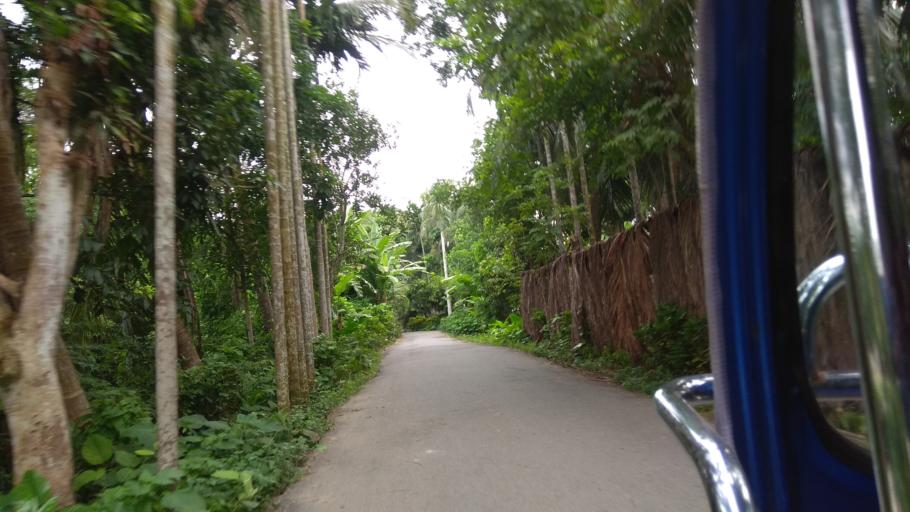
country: BD
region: Khulna
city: Kalia
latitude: 23.0381
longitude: 89.6590
